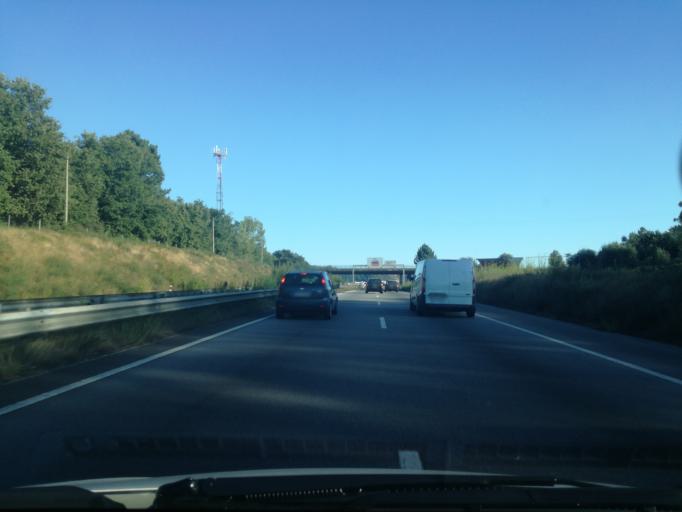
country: PT
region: Braga
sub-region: Braga
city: Braga
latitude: 41.5846
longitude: -8.4360
